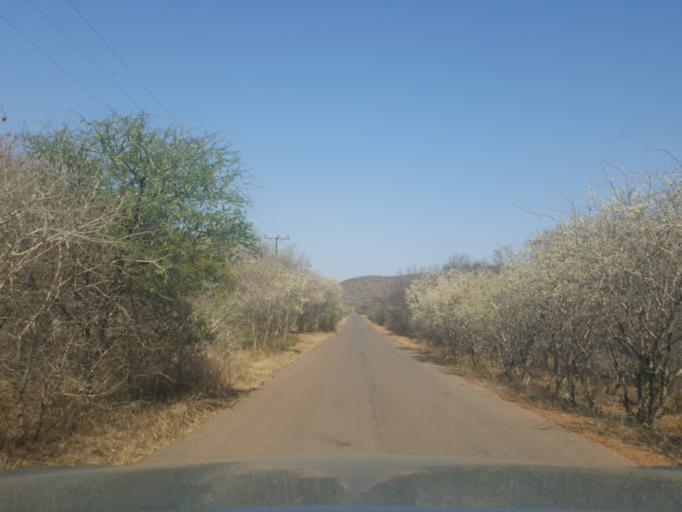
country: BW
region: Kweneng
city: Gabane
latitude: -24.7413
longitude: 25.8213
